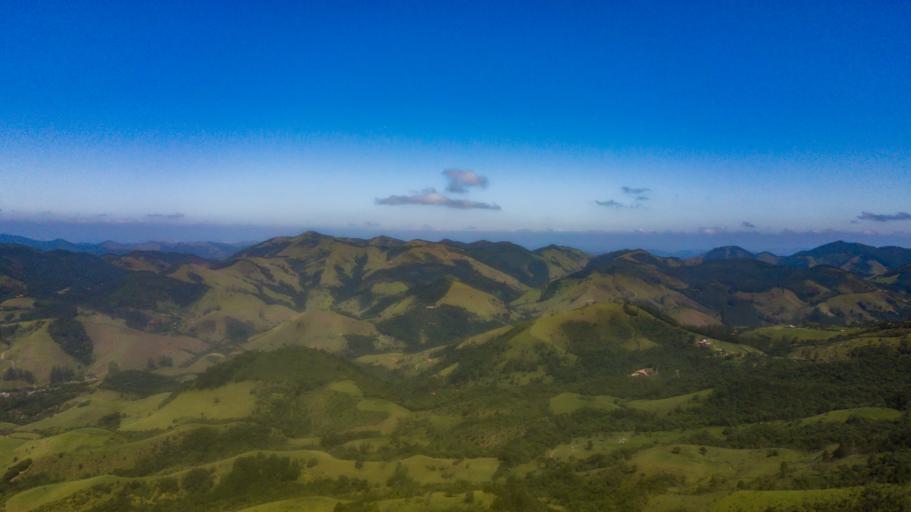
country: BR
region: Minas Gerais
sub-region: Camanducaia
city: Camanducaia
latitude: -22.8917
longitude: -45.9745
